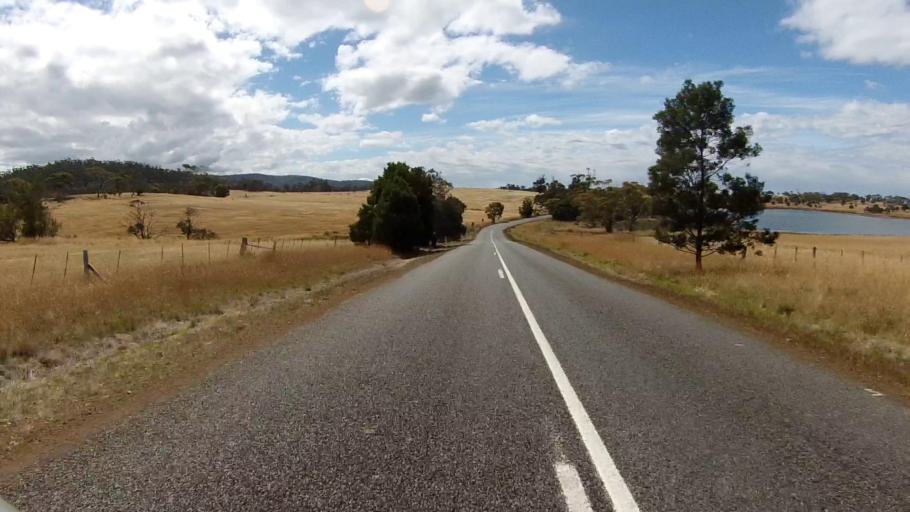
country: AU
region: Tasmania
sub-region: Sorell
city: Sorell
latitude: -42.2821
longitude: 147.9989
